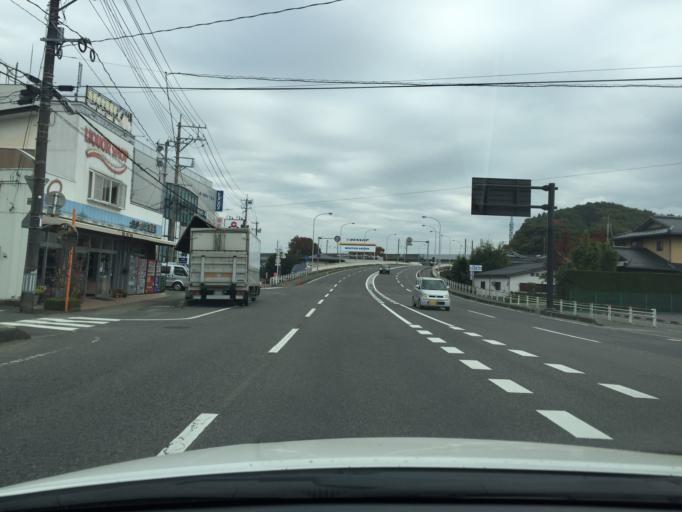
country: JP
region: Tochigi
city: Kuroiso
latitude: 37.1310
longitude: 140.1918
